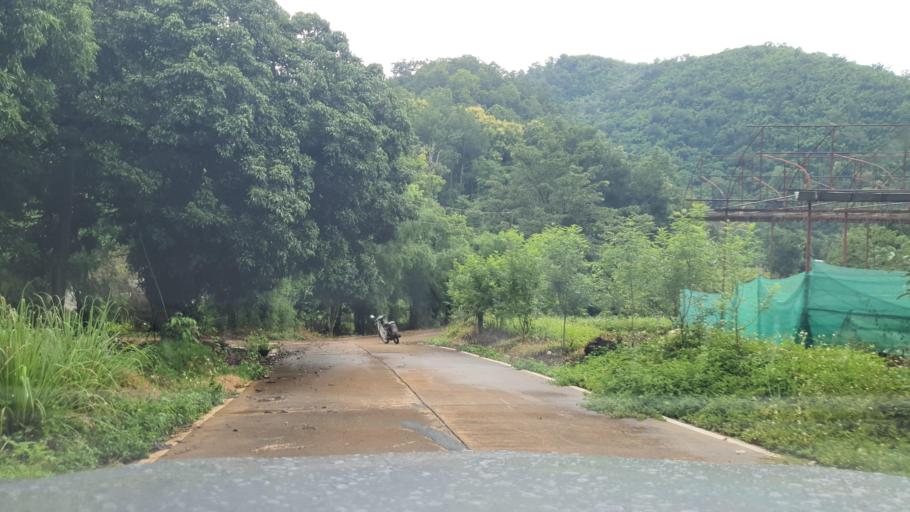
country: TH
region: Chiang Mai
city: Samoeng
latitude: 18.8339
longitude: 98.7752
